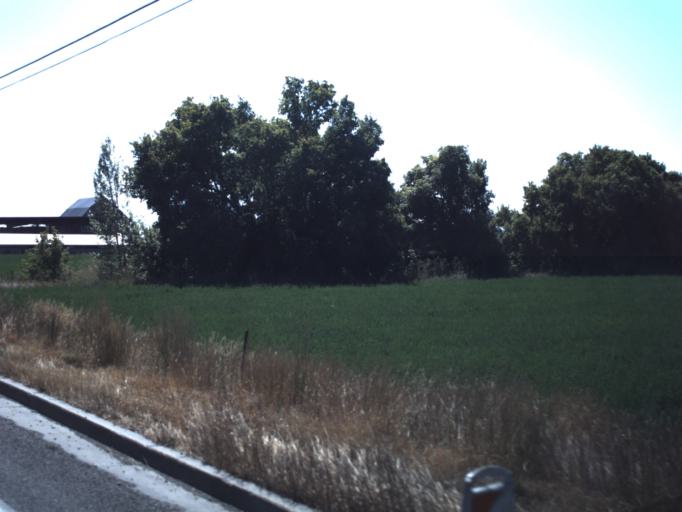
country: US
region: Utah
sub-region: Cache County
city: Richmond
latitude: 41.9182
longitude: -111.8145
